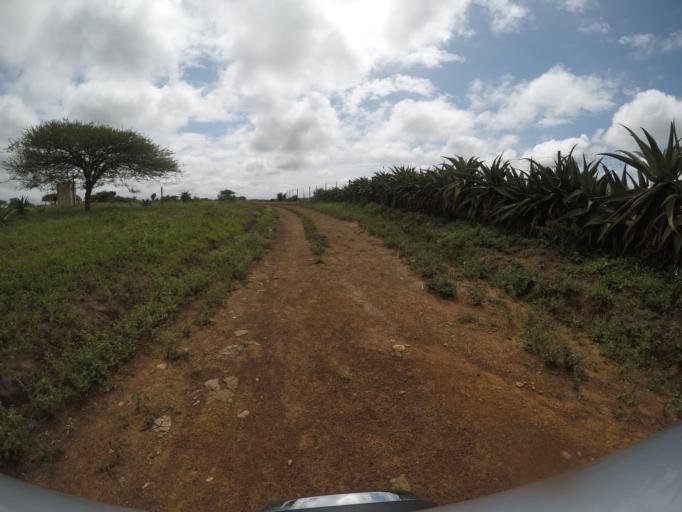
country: ZA
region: KwaZulu-Natal
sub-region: uThungulu District Municipality
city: Empangeni
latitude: -28.5822
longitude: 31.8508
